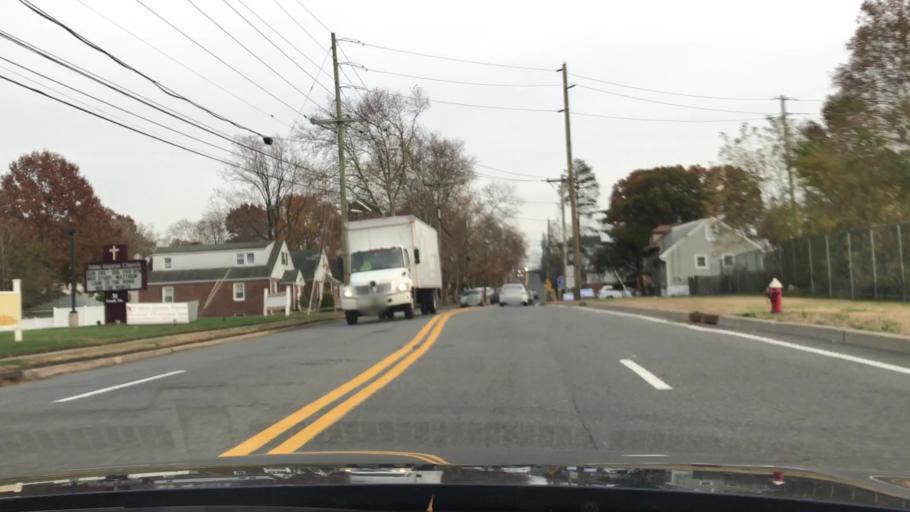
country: US
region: New Jersey
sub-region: Bergen County
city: Hasbrouck Heights
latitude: 40.8610
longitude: -74.0868
